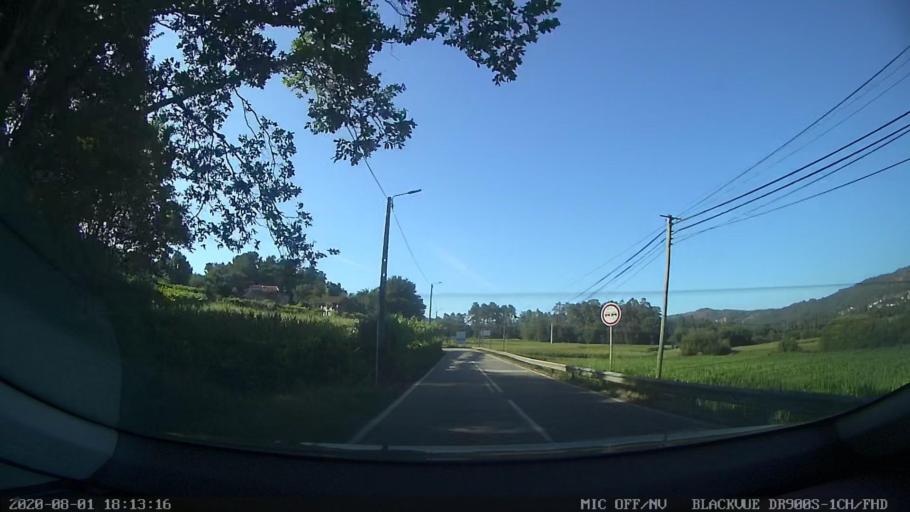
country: PT
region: Porto
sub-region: Pacos de Ferreira
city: Seroa
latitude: 41.2817
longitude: -8.4701
